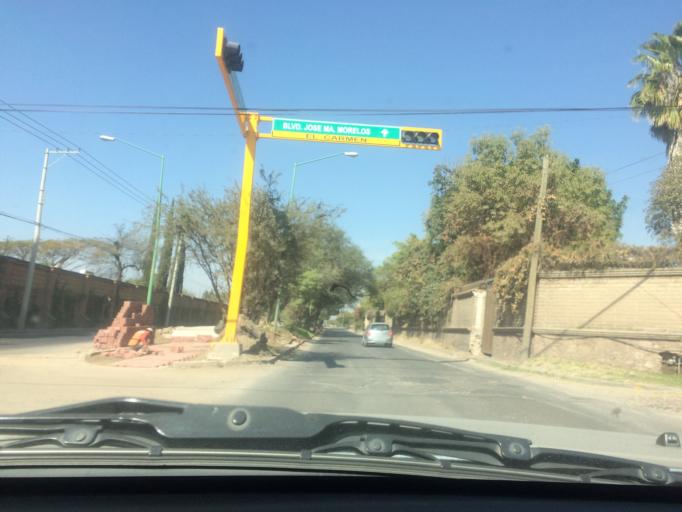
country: MX
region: Guanajuato
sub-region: Leon
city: Fraccionamiento Paraiso Real
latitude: 21.1178
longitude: -101.6098
